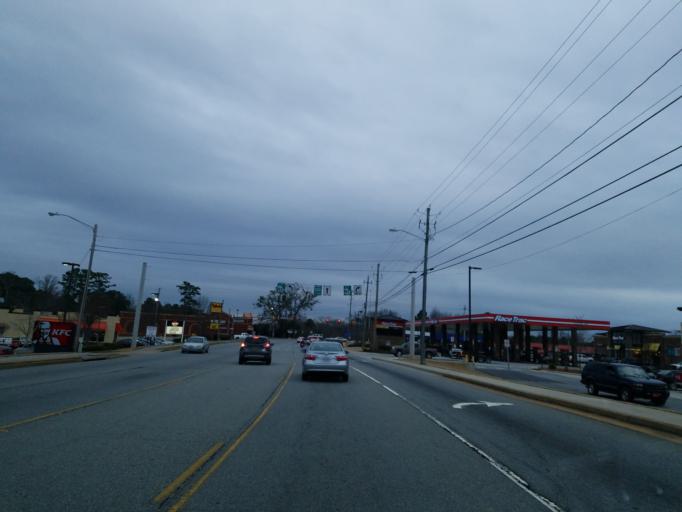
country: US
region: Georgia
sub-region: Cobb County
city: Acworth
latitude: 34.0752
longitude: -84.6770
